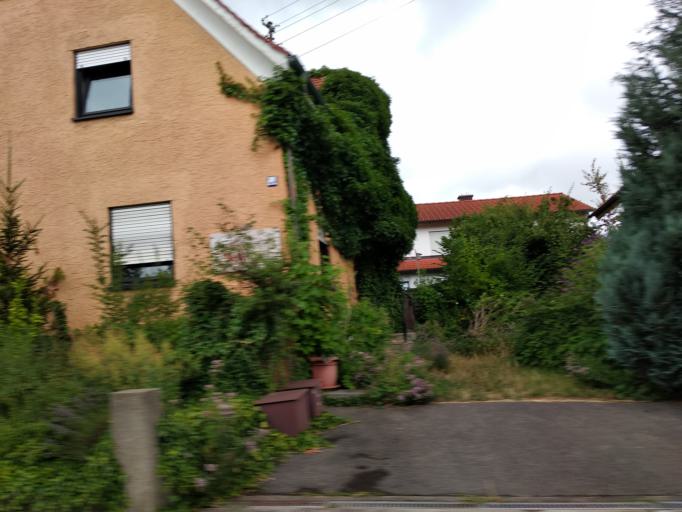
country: DE
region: Bavaria
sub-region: Swabia
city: Benningen
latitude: 47.9693
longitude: 10.2115
